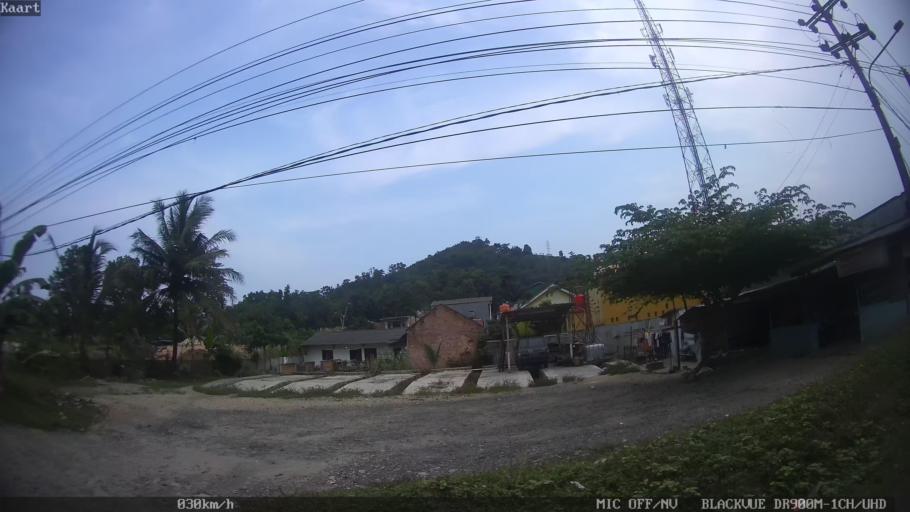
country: ID
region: Lampung
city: Panjang
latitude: -5.4186
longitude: 105.3301
